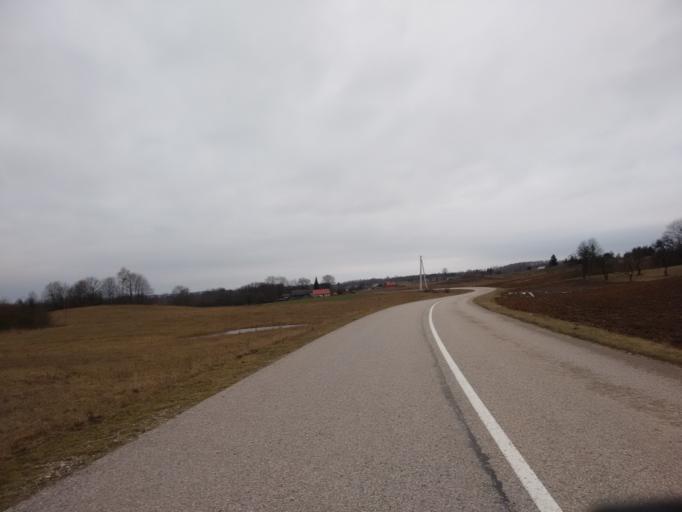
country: LT
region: Alytaus apskritis
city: Druskininkai
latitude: 54.2239
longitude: 23.8942
